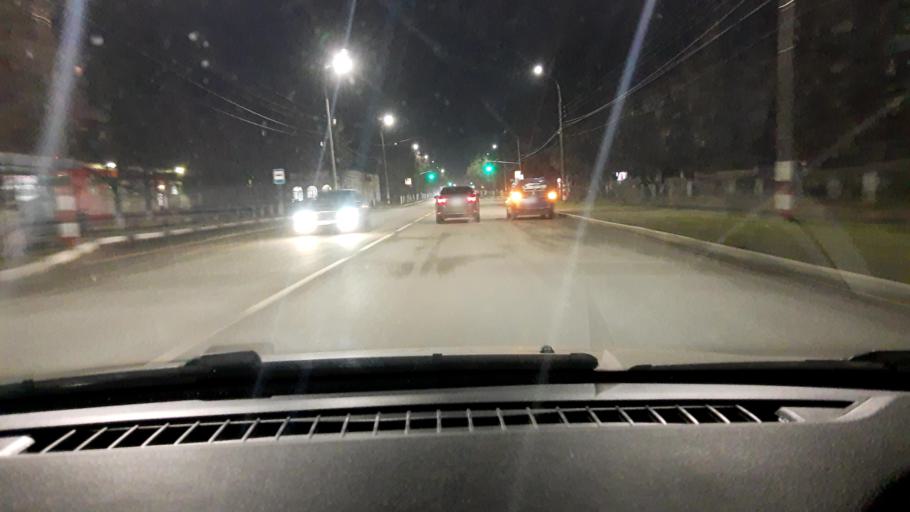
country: RU
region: Nizjnij Novgorod
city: Dzerzhinsk
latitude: 56.2541
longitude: 43.4663
